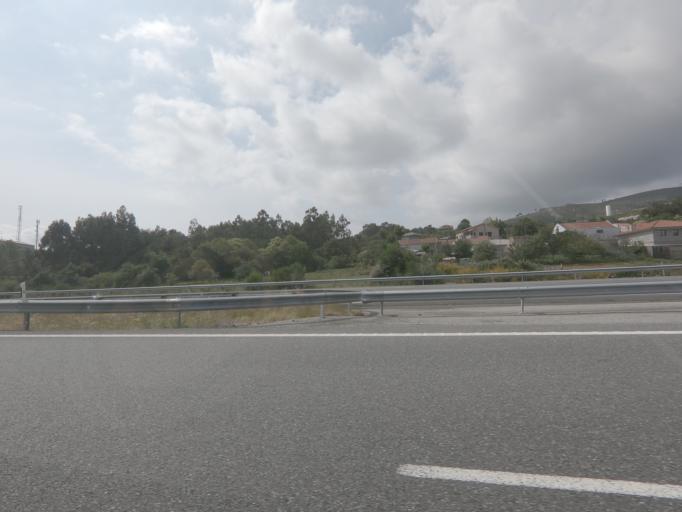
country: ES
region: Galicia
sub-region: Provincia de Ourense
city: Melon
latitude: 42.2173
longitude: -8.2560
